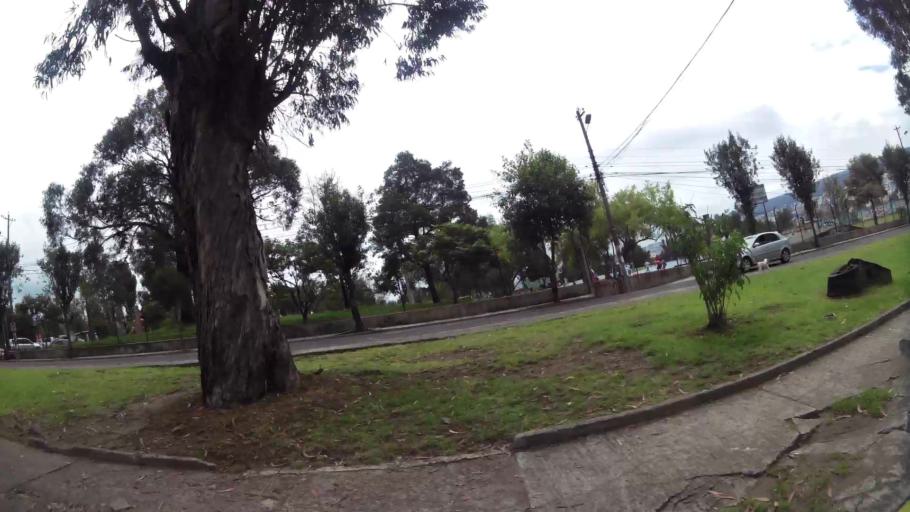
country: EC
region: Pichincha
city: Quito
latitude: -0.1854
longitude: -78.4983
